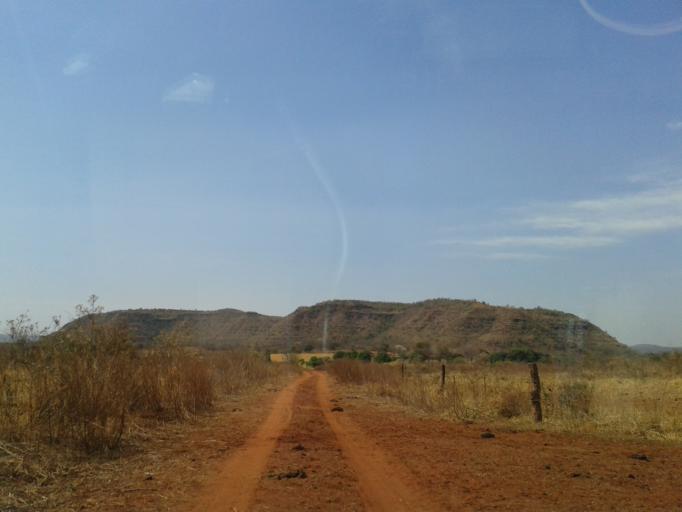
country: BR
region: Minas Gerais
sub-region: Santa Vitoria
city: Santa Vitoria
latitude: -19.2066
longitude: -50.0284
